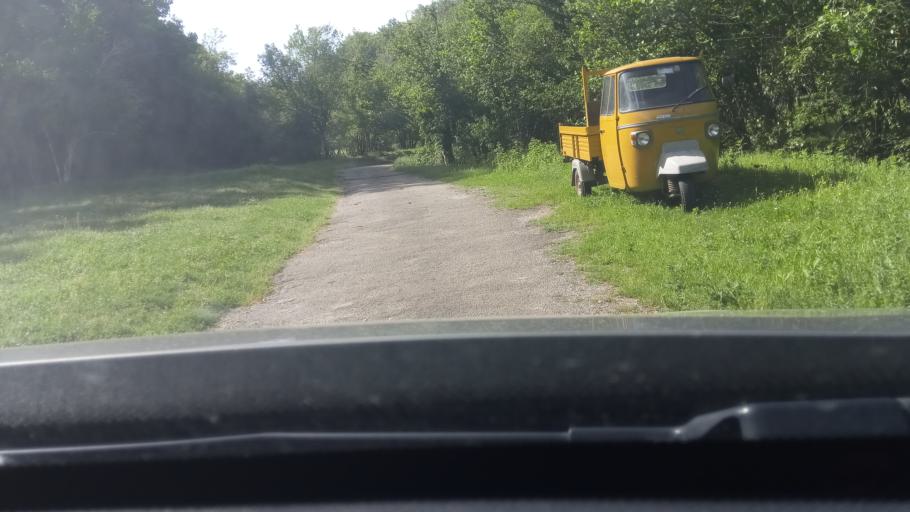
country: IT
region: Latium
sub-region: Provincia di Latina
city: Minturno
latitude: 41.2765
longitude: 13.7657
